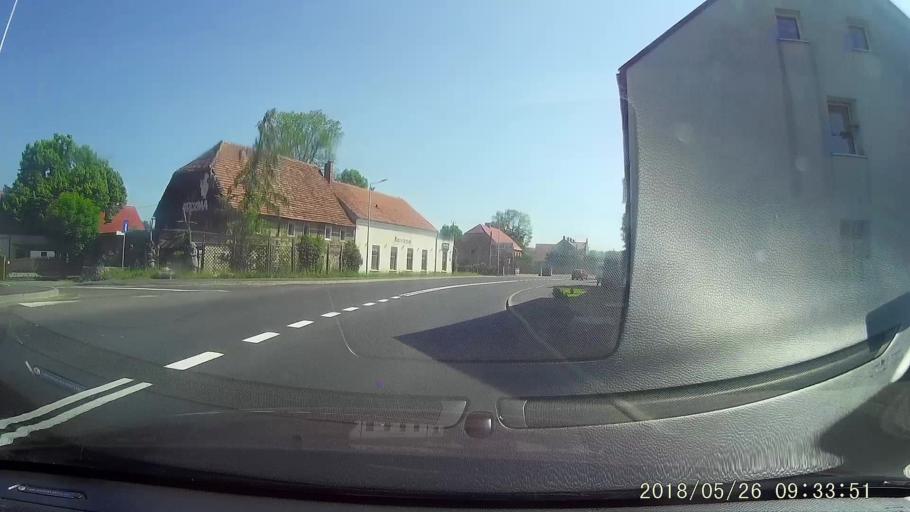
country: PL
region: Lower Silesian Voivodeship
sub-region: Powiat zgorzelecki
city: Lagow
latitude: 51.1587
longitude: 15.0446
